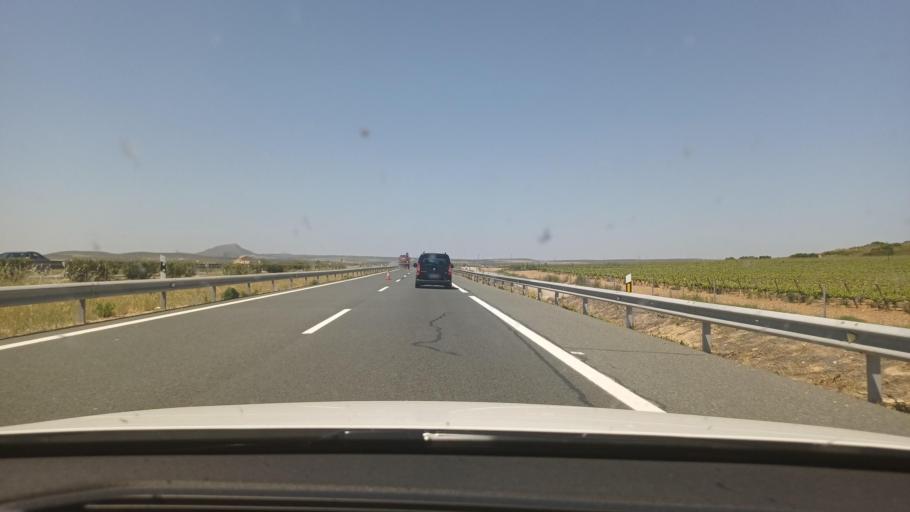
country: ES
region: Castille-La Mancha
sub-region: Provincia de Albacete
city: Alpera
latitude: 38.8796
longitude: -1.2081
